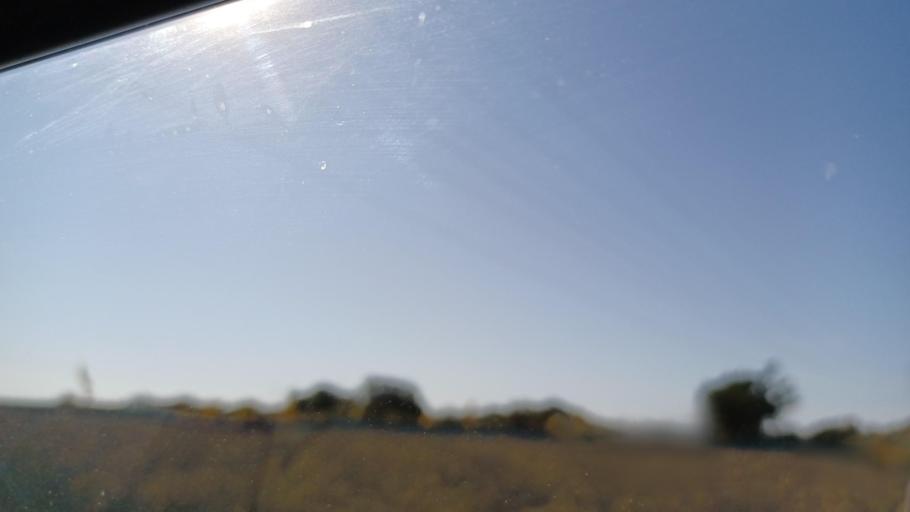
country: CY
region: Larnaka
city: Kolossi
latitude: 34.6616
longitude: 32.9358
